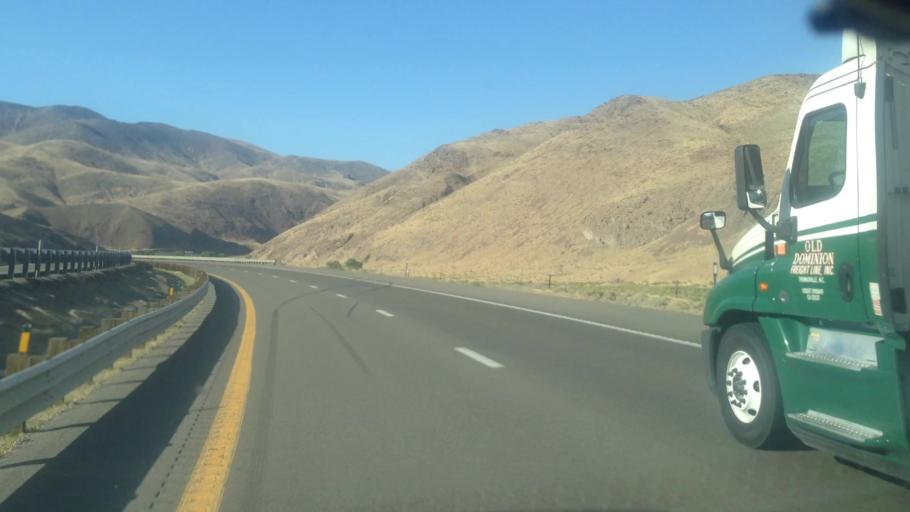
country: US
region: Nevada
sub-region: Lyon County
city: Stagecoach
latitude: 39.5703
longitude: -119.4729
